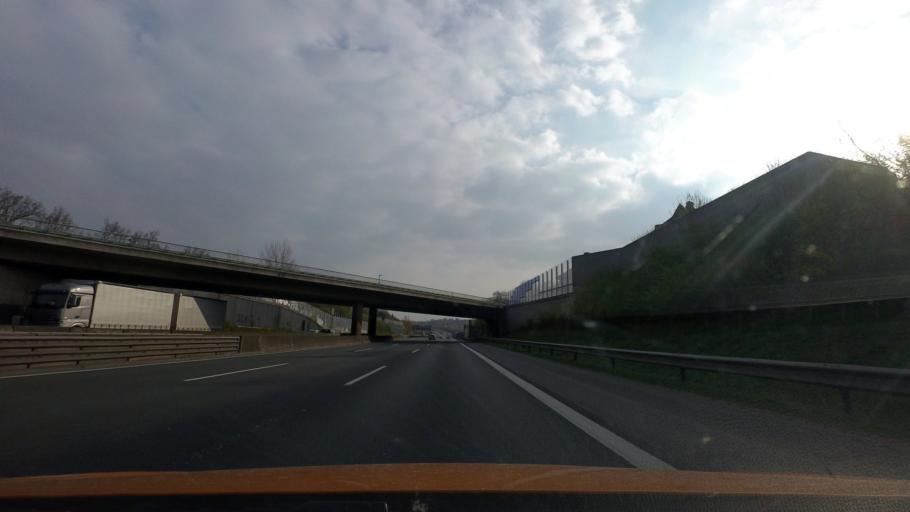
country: DE
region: North Rhine-Westphalia
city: Bad Oeynhausen
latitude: 52.1997
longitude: 8.8312
